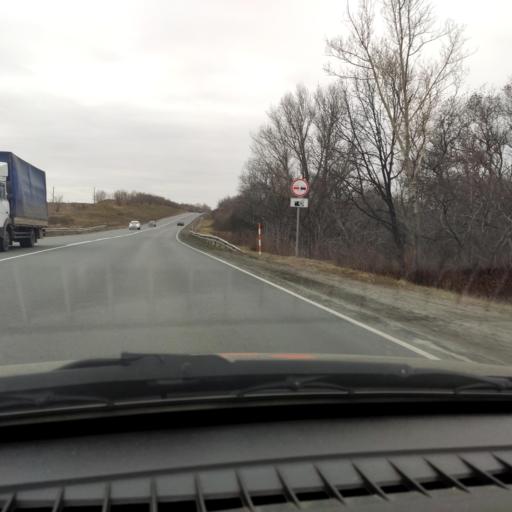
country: RU
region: Samara
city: Zhigulevsk
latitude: 53.3600
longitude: 49.4575
